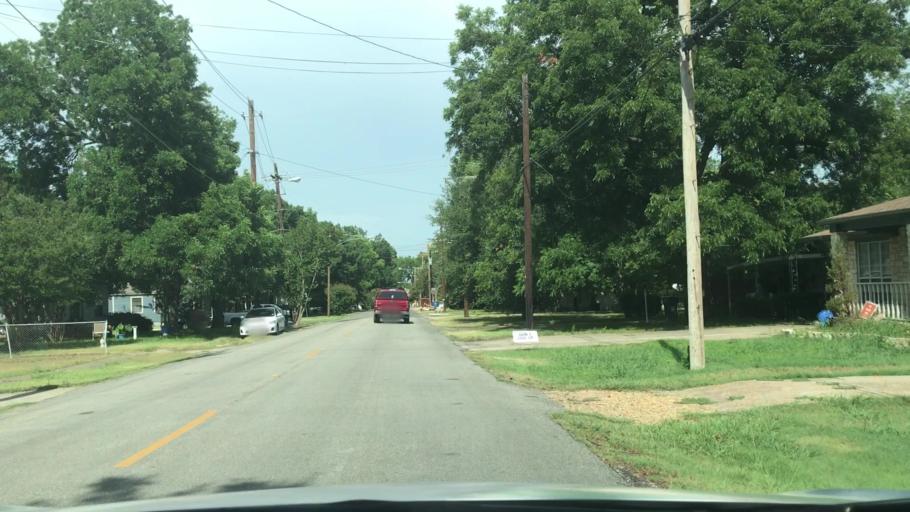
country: US
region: Texas
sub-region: Dallas County
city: Highland Park
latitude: 32.8450
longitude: -96.7502
